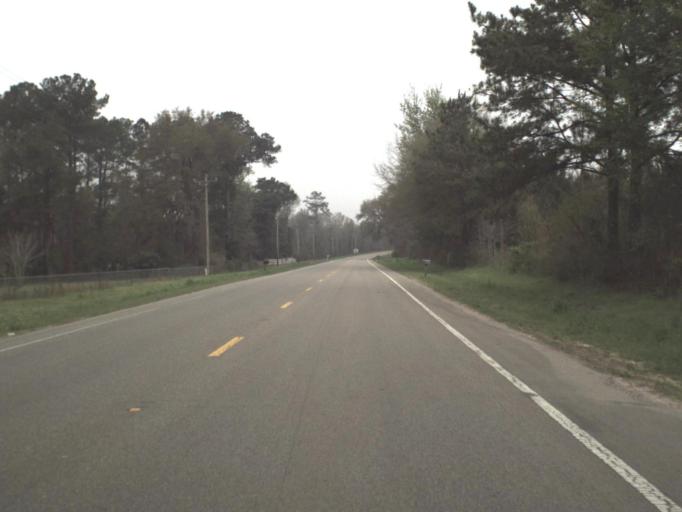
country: US
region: Florida
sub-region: Gadsden County
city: Gretna
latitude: 30.5828
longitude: -84.6726
